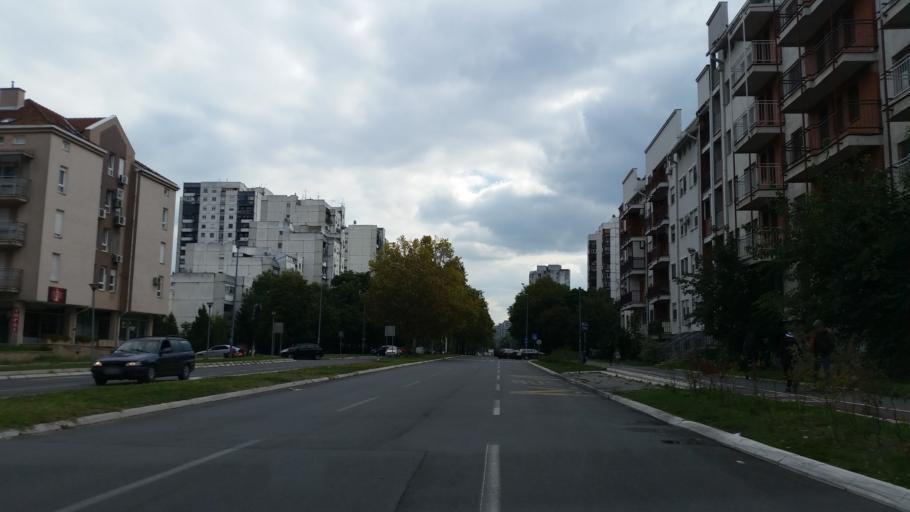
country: RS
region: Central Serbia
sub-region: Belgrade
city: Zemun
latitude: 44.8102
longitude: 20.3826
